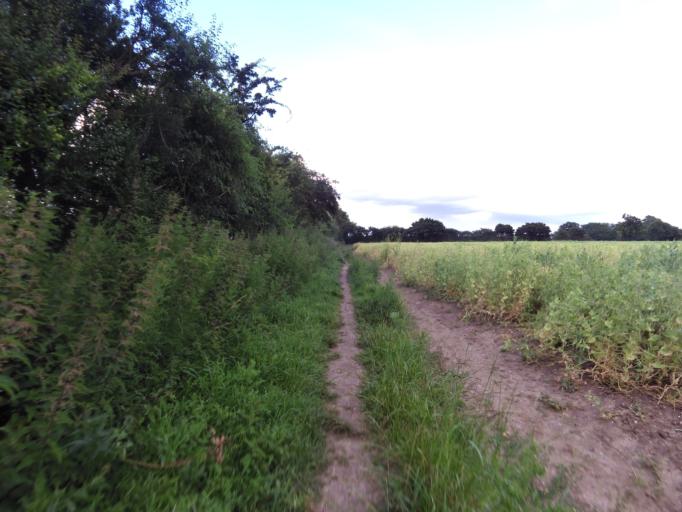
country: GB
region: England
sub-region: Suffolk
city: Ipswich
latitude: 52.0765
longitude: 1.1575
